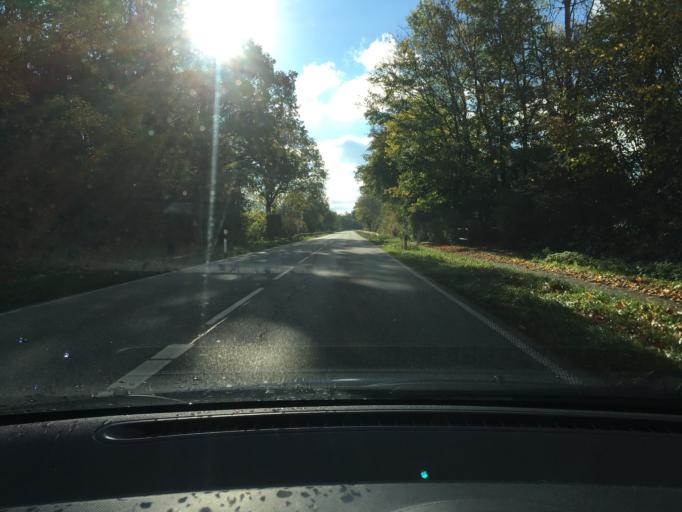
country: DE
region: Schleswig-Holstein
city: Busdorf
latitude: 54.4985
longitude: 9.5544
